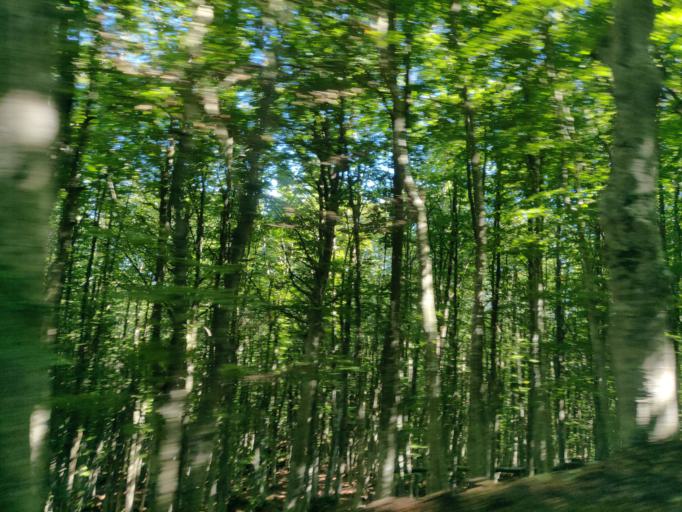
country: IT
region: Tuscany
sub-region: Provincia di Siena
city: Abbadia San Salvatore
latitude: 42.8914
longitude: 11.6327
